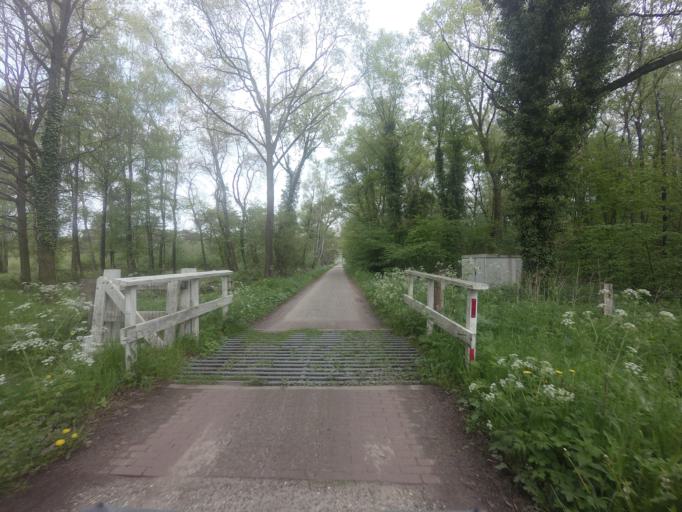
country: NL
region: Overijssel
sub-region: Gemeente Haaksbergen
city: Haaksbergen
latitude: 52.1846
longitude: 6.8146
